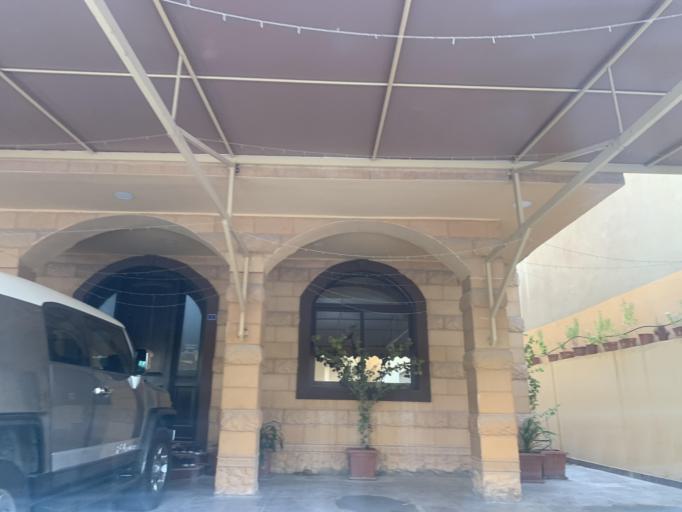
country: BH
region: Manama
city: Jidd Hafs
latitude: 26.1971
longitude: 50.5304
